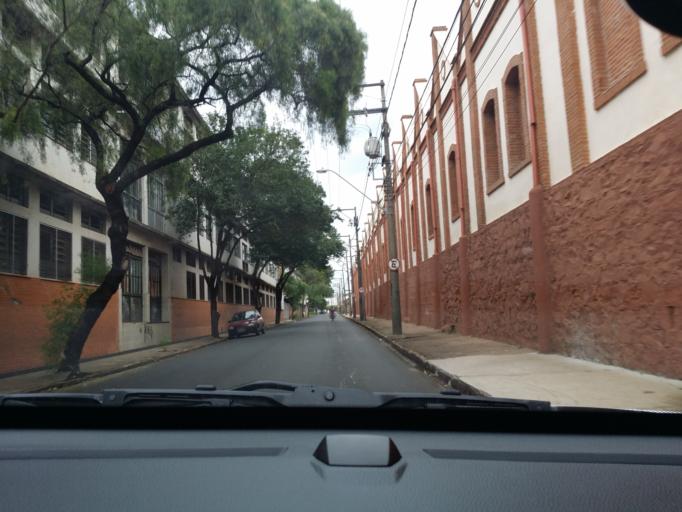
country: BR
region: Sao Paulo
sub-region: Sao Carlos
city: Sao Carlos
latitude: -22.0243
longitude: -47.8935
